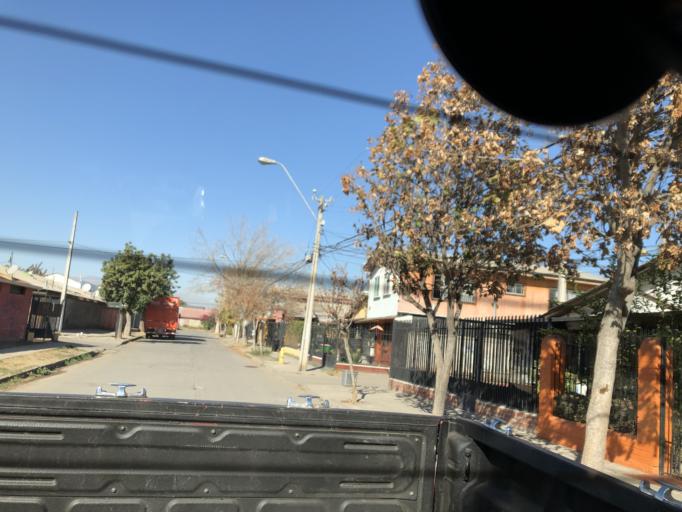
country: CL
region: Santiago Metropolitan
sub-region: Provincia de Cordillera
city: Puente Alto
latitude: -33.5723
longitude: -70.5747
